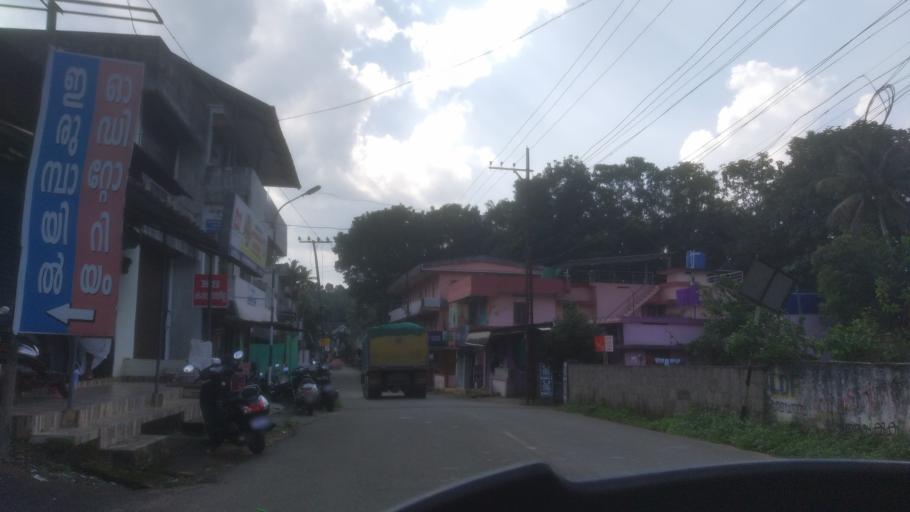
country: IN
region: Kerala
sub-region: Ernakulam
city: Kotamangalam
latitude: 10.0063
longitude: 76.6801
